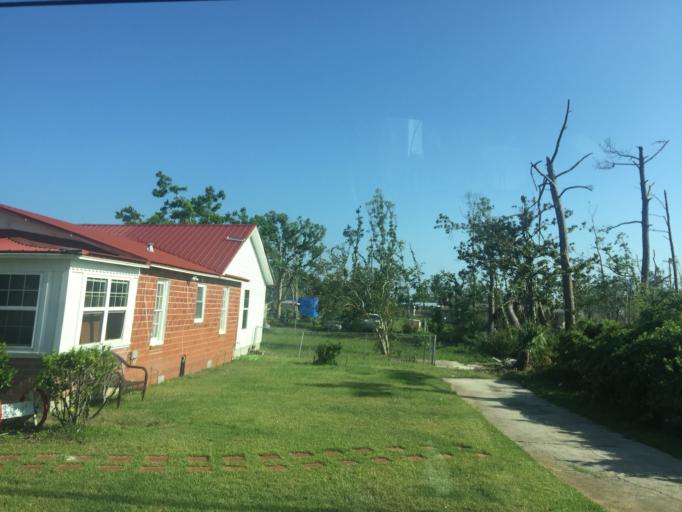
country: US
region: Florida
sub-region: Bay County
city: Cedar Grove
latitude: 30.1604
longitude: -85.6360
